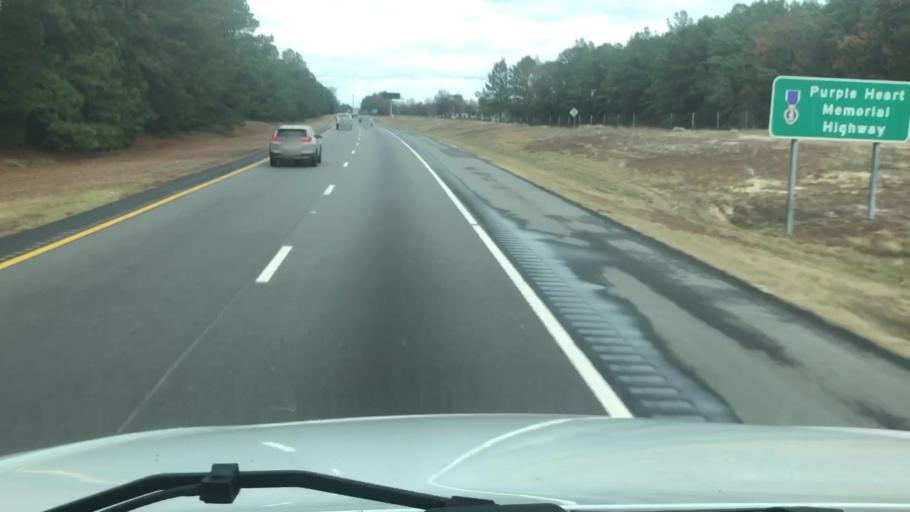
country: US
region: North Carolina
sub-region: Cumberland County
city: Vander
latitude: 35.0606
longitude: -78.7944
